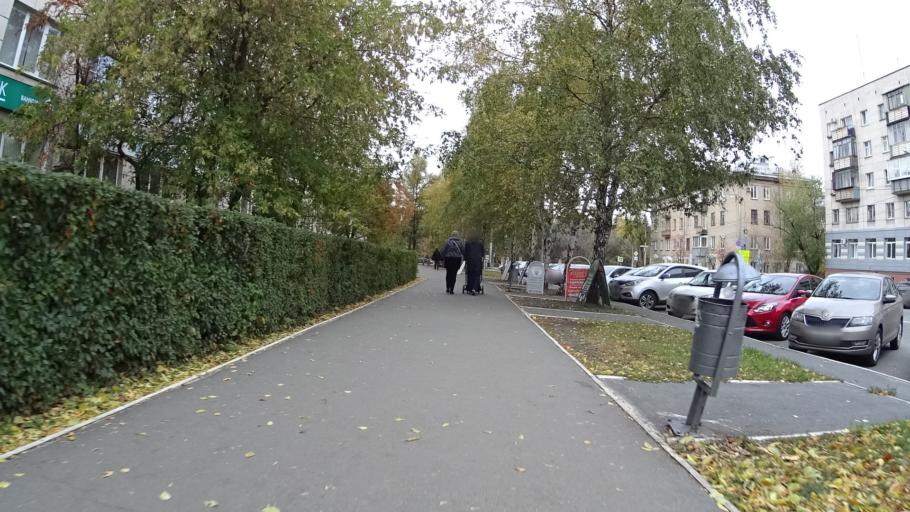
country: RU
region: Chelyabinsk
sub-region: Gorod Chelyabinsk
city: Chelyabinsk
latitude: 55.1610
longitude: 61.3752
